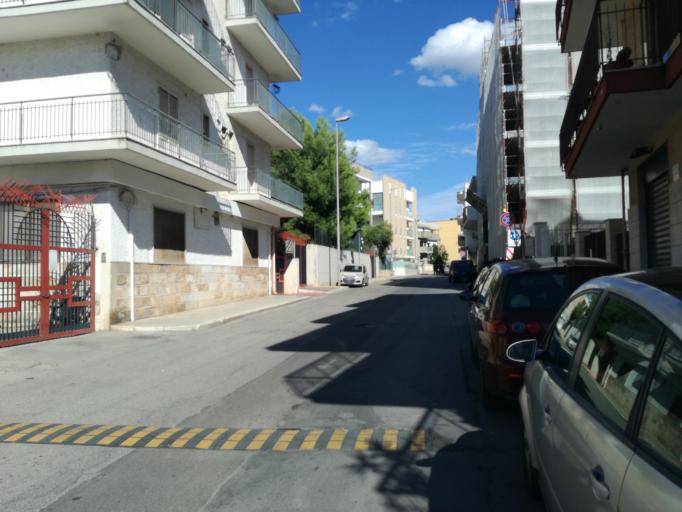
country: IT
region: Apulia
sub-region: Provincia di Bari
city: Triggiano
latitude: 41.0672
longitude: 16.9344
